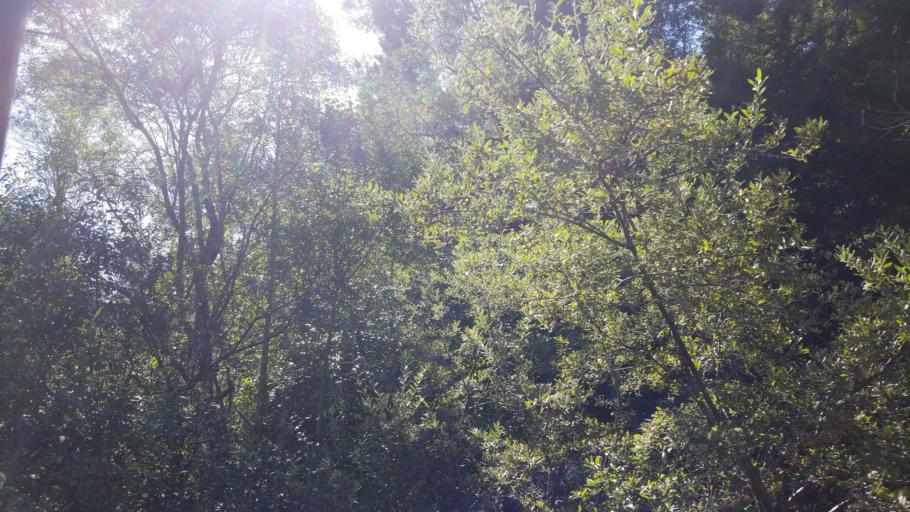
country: US
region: California
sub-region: Mendocino County
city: Fort Bragg
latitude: 39.4489
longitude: -123.7825
